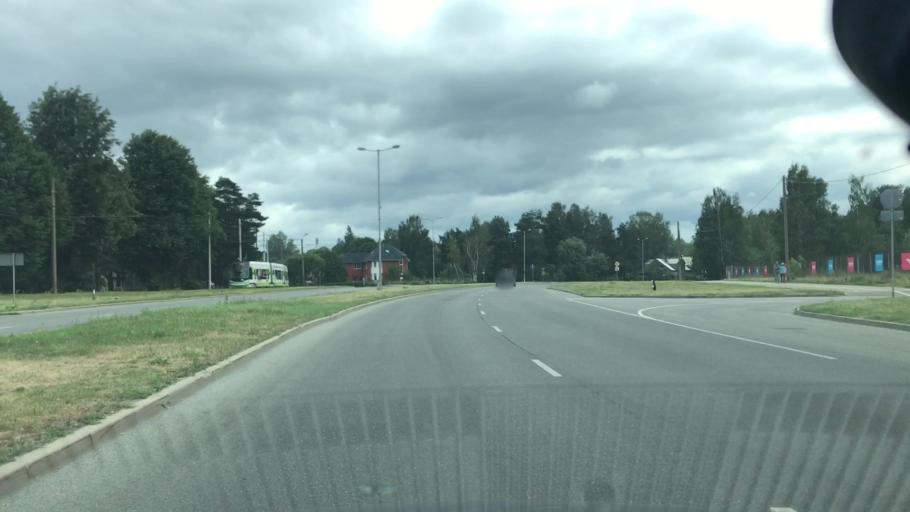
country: LV
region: Marupe
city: Marupe
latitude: 56.9587
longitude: 24.0223
